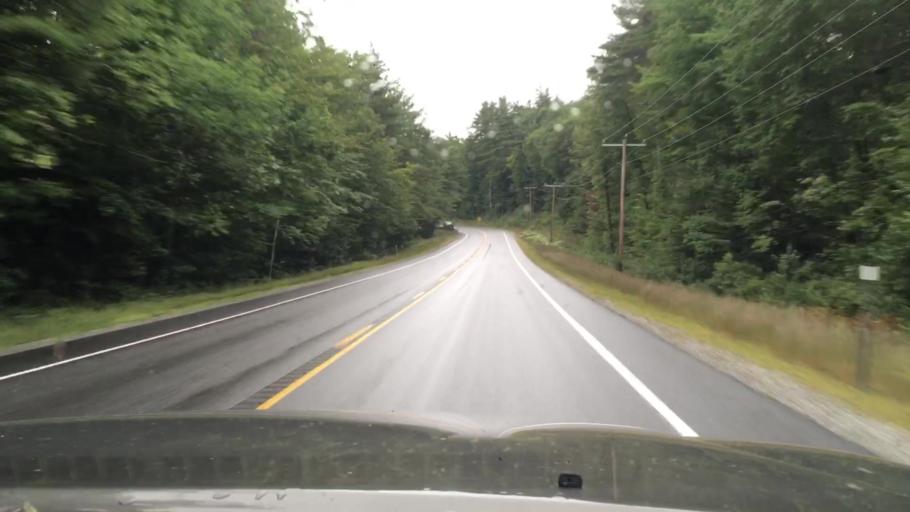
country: US
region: New Hampshire
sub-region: Hillsborough County
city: Antrim
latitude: 43.0926
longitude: -71.9663
